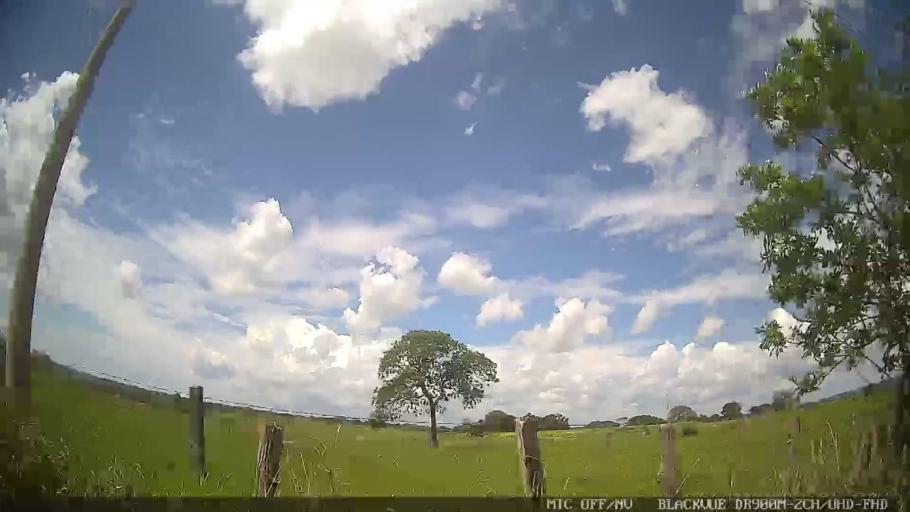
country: BR
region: Sao Paulo
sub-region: Conchas
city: Conchas
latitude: -23.0489
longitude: -47.9906
